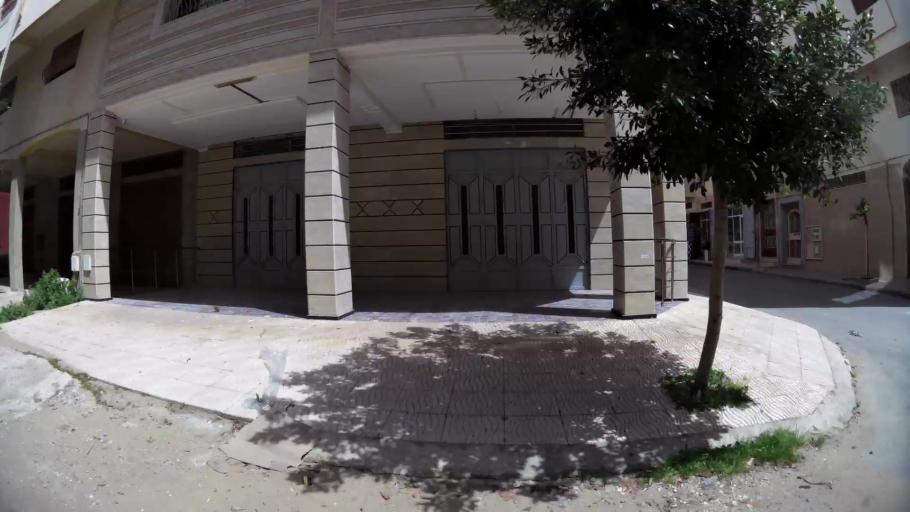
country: MA
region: Tanger-Tetouan
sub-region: Tanger-Assilah
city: Tangier
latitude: 35.7572
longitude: -5.8392
